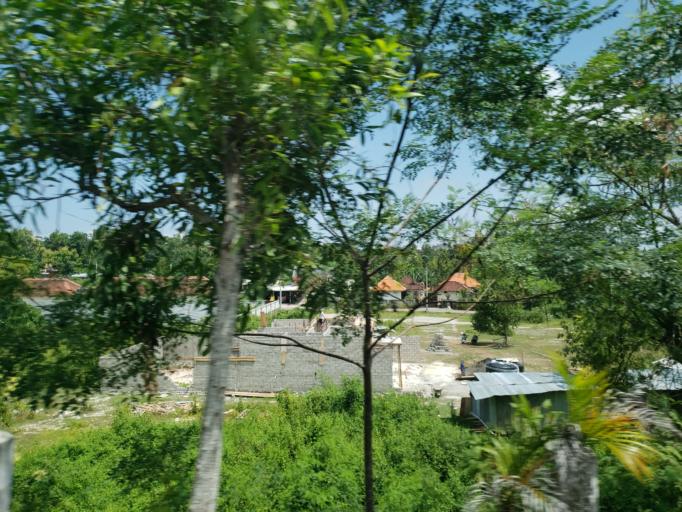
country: ID
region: Bali
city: Kangin
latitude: -8.8244
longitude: 115.1449
